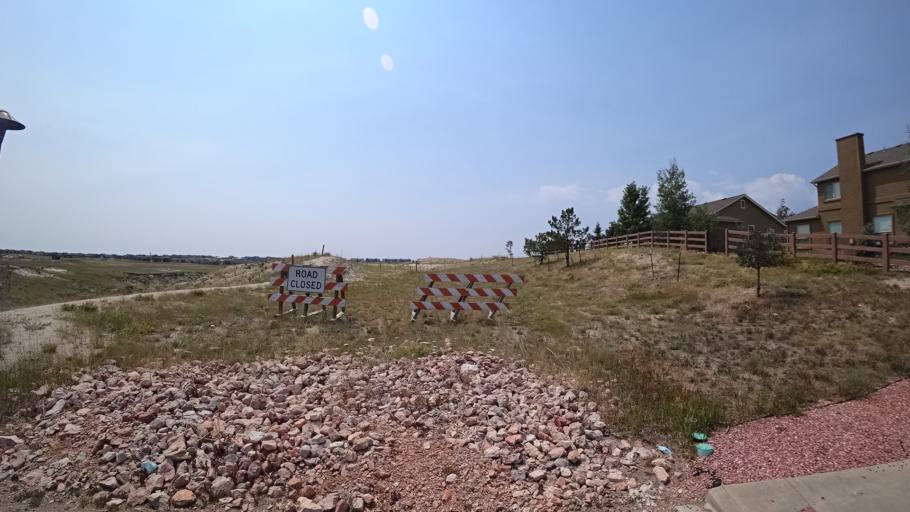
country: US
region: Colorado
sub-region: El Paso County
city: Black Forest
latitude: 38.9589
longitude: -104.7132
